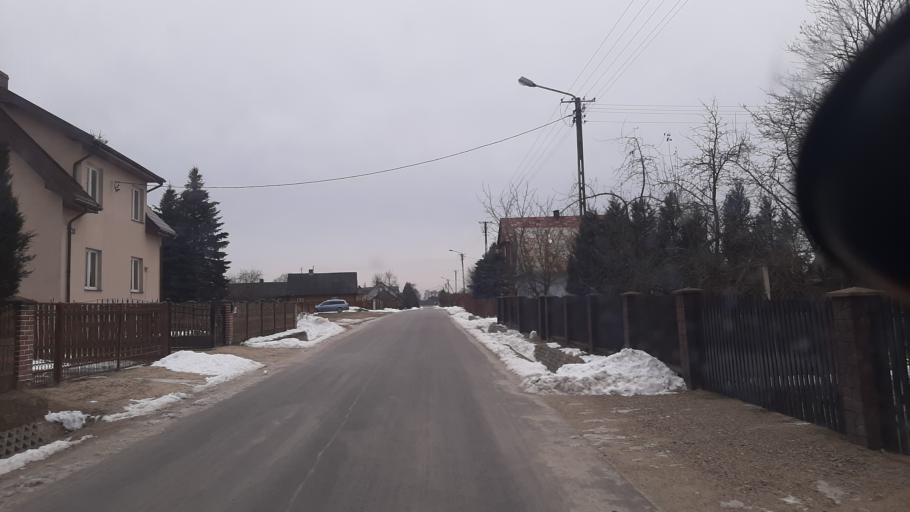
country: PL
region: Lublin Voivodeship
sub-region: Powiat lubartowski
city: Kamionka
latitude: 51.5163
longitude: 22.4735
